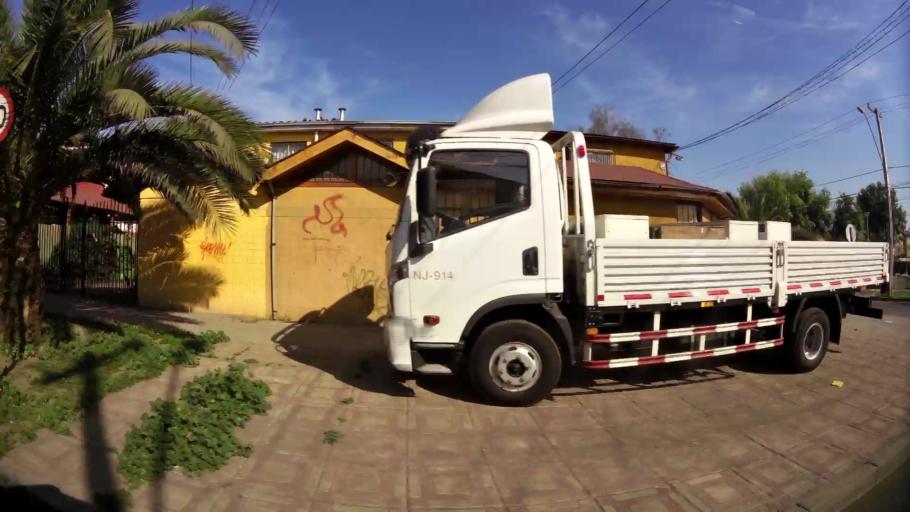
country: CL
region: Santiago Metropolitan
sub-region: Provincia de Santiago
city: Lo Prado
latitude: -33.4602
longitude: -70.7609
